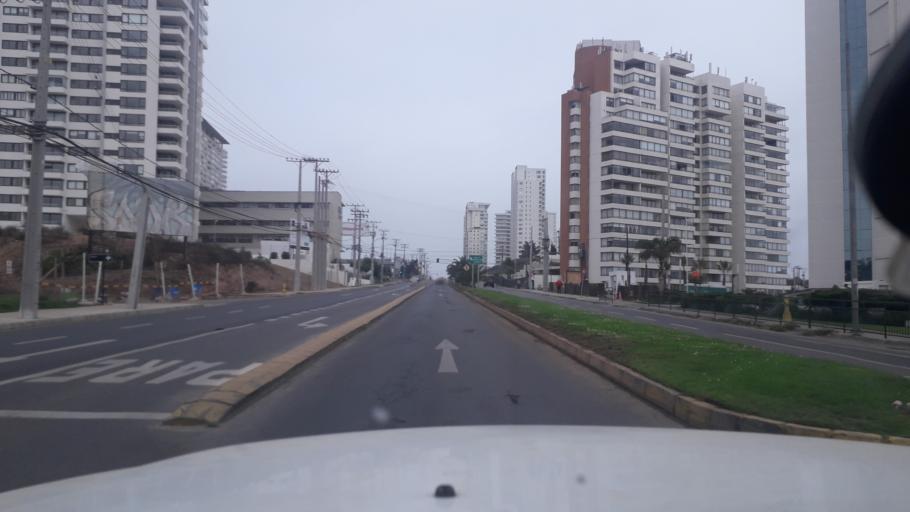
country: CL
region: Valparaiso
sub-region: Provincia de Valparaiso
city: Vina del Mar
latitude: -32.9551
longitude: -71.5440
